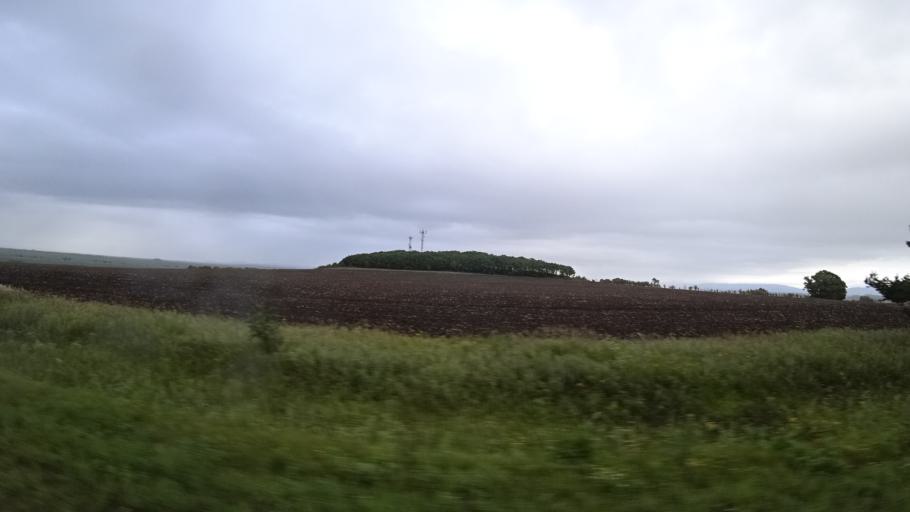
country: RU
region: Primorskiy
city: Chernigovka
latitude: 44.3680
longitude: 132.5331
